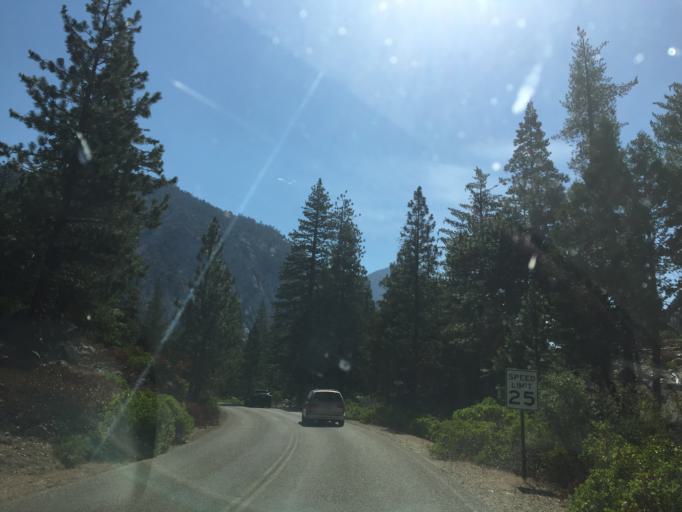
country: US
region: California
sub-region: Tulare County
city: Three Rivers
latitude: 36.7938
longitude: -118.5876
